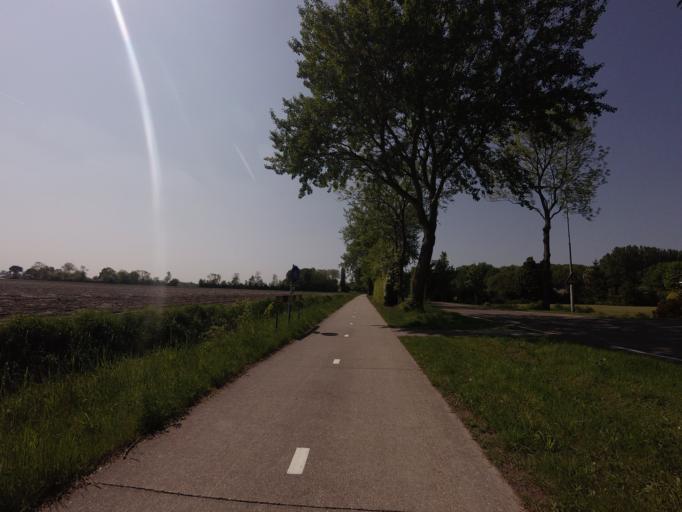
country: NL
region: Zeeland
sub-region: Gemeente Veere
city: Veere
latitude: 51.5459
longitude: 3.6472
